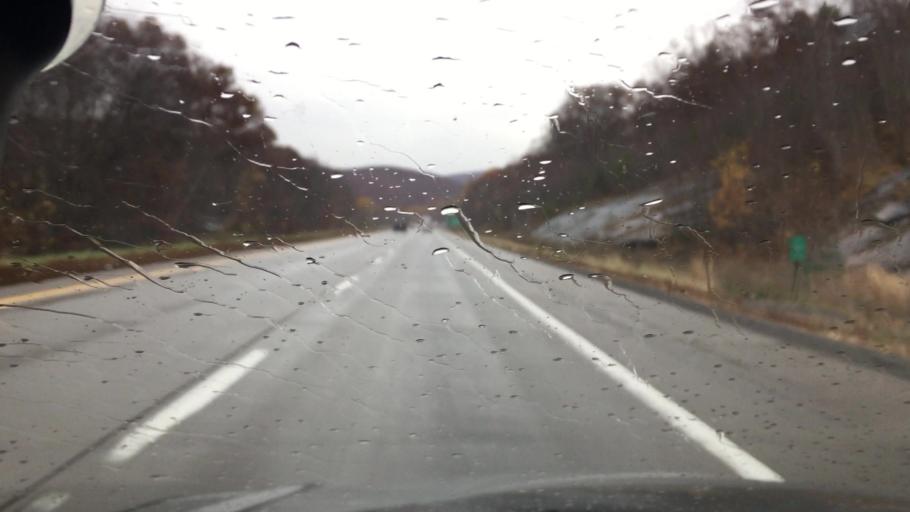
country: US
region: Pennsylvania
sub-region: Luzerne County
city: Ashley
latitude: 41.1806
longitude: -75.9326
